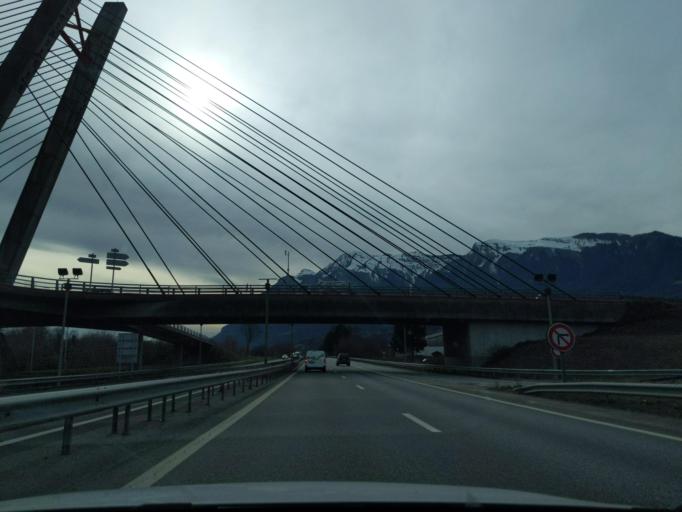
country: FR
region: Rhone-Alpes
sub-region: Departement de la Savoie
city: Gilly-sur-Isere
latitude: 45.6530
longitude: 6.3581
